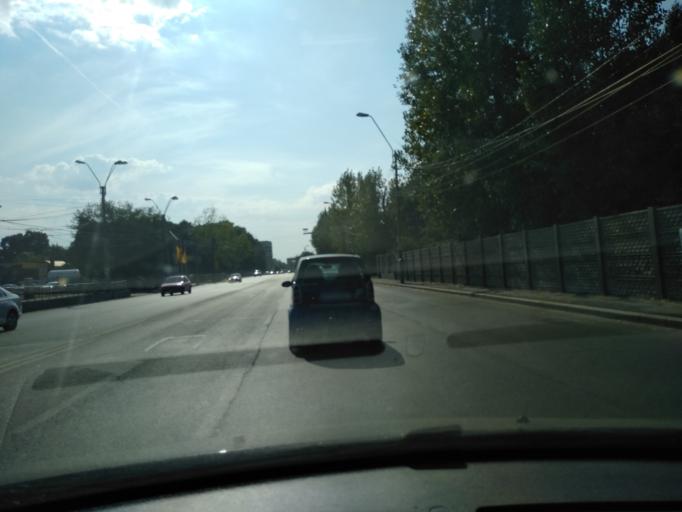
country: RO
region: Ilfov
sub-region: Comuna Popesti-Leordeni
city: Popesti-Leordeni
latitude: 44.3835
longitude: 26.1459
